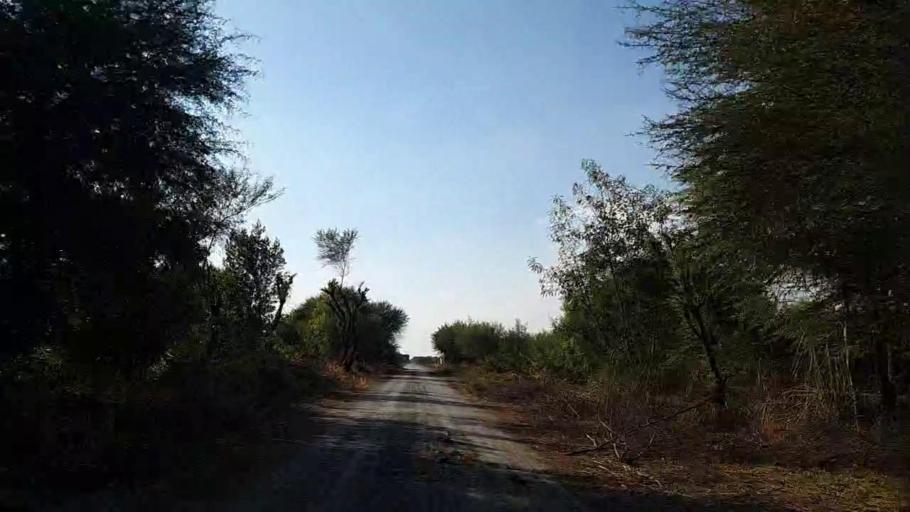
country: PK
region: Sindh
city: Pithoro
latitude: 25.6483
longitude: 69.3122
